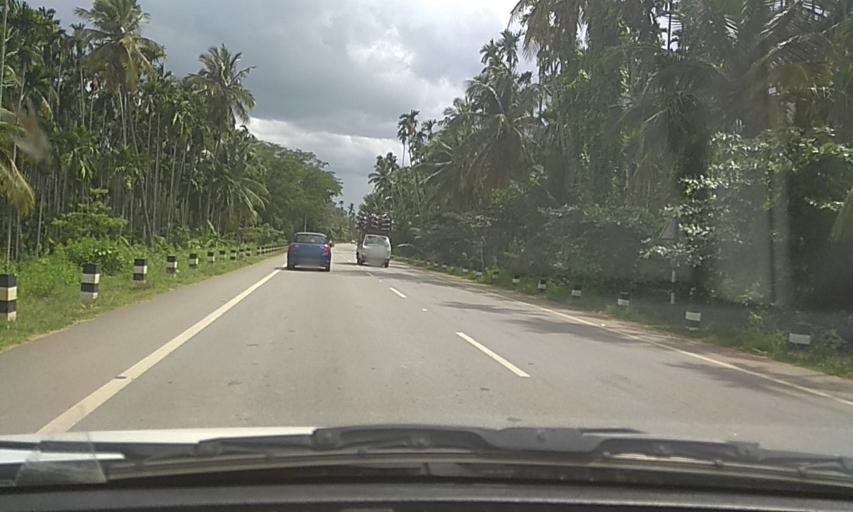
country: IN
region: Karnataka
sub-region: Tumkur
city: Tumkur
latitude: 13.2115
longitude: 77.0543
